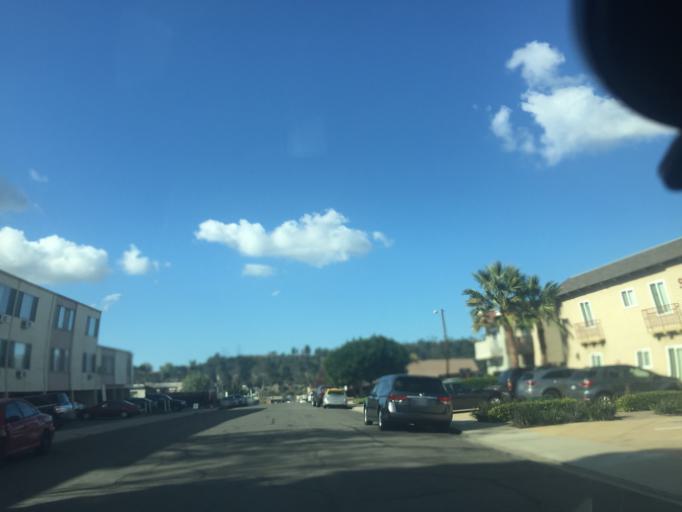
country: US
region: California
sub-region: San Diego County
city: La Mesa
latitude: 32.7892
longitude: -117.0958
